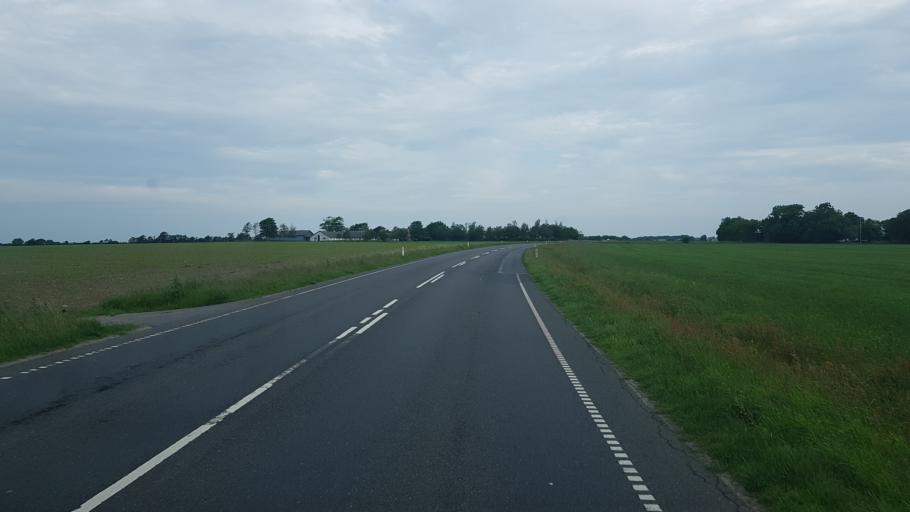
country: DK
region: South Denmark
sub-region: Vejen Kommune
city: Rodding
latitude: 55.4010
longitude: 9.0337
